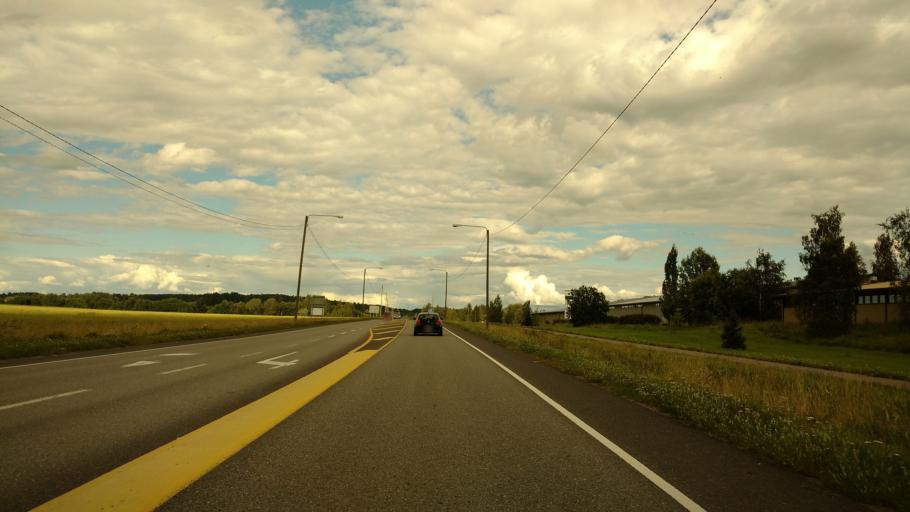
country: FI
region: Varsinais-Suomi
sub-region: Salo
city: Halikko
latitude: 60.3873
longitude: 23.0637
